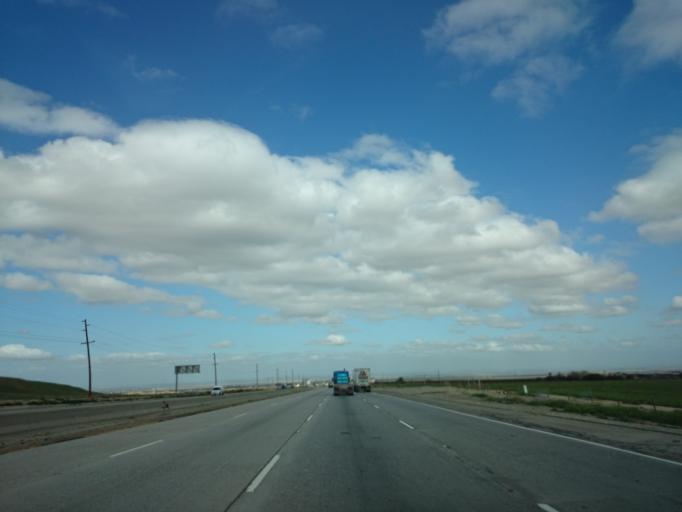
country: US
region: California
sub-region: Kern County
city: Frazier Park
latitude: 34.9991
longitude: -118.9492
